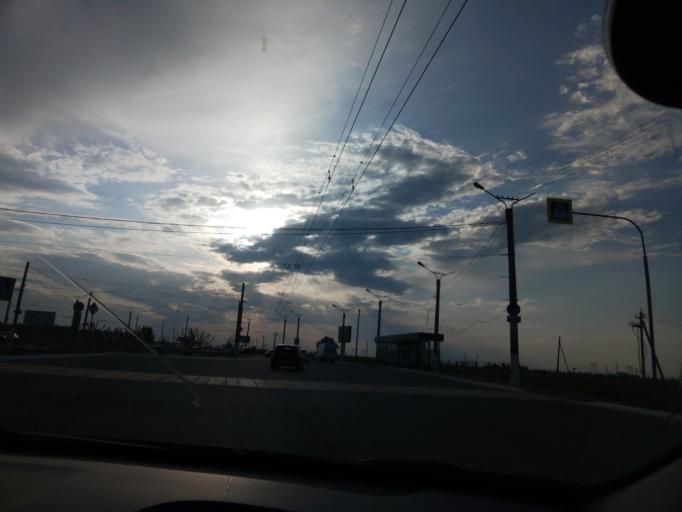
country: RU
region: Chuvashia
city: Novocheboksarsk
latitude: 56.1205
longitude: 47.4466
